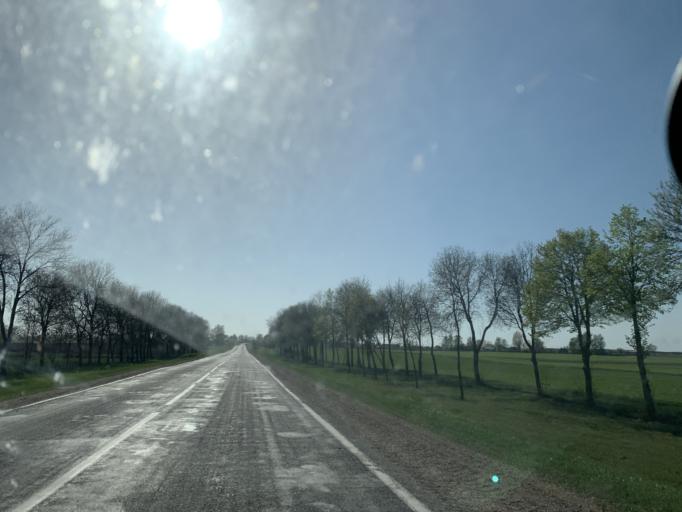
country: BY
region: Minsk
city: Nyasvizh
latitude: 53.2289
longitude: 26.7750
